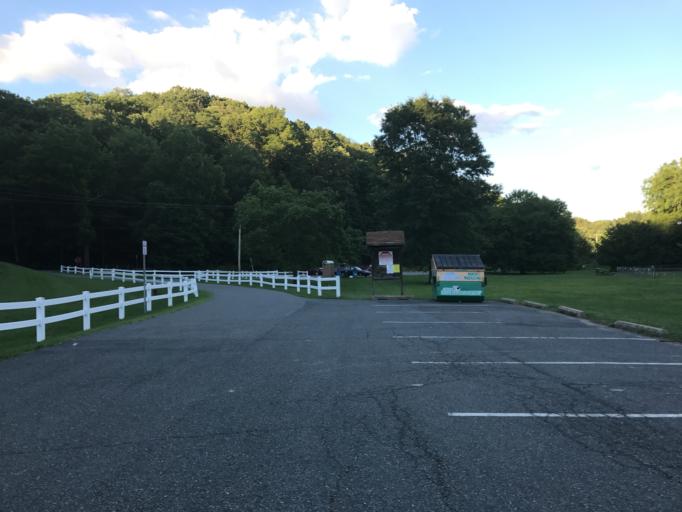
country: US
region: Maryland
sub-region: Harford County
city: Jarrettsville
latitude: 39.6755
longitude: -76.4506
